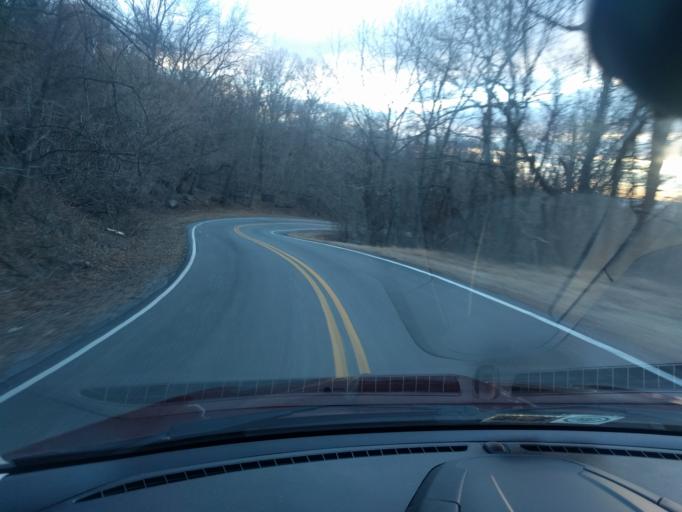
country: US
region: Virginia
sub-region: City of Bedford
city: Bedford
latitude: 37.4346
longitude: -79.5828
